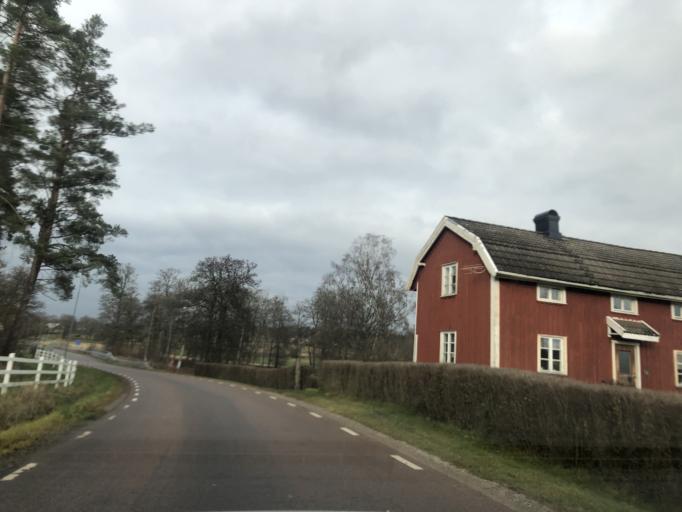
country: SE
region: Vaestra Goetaland
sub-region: Boras Kommun
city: Dalsjofors
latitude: 57.8261
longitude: 13.1584
